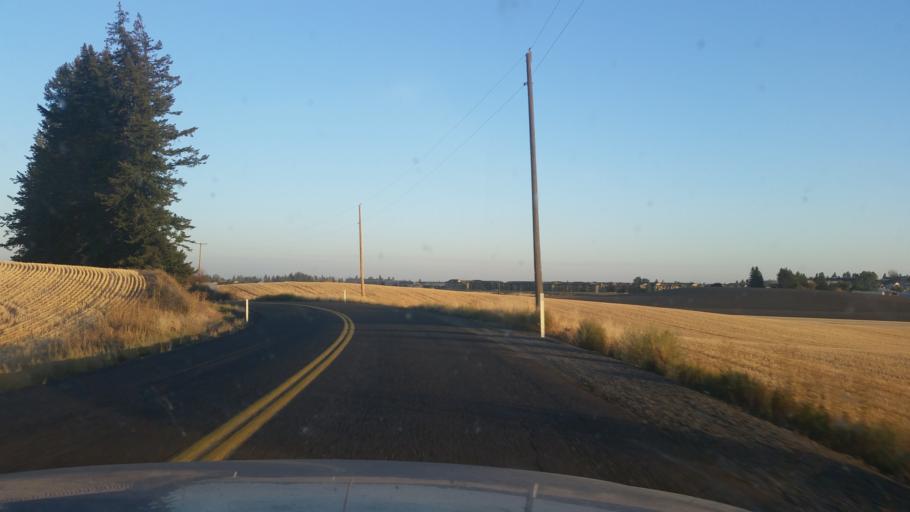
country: US
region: Washington
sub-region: Spokane County
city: Cheney
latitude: 47.5130
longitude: -117.5905
